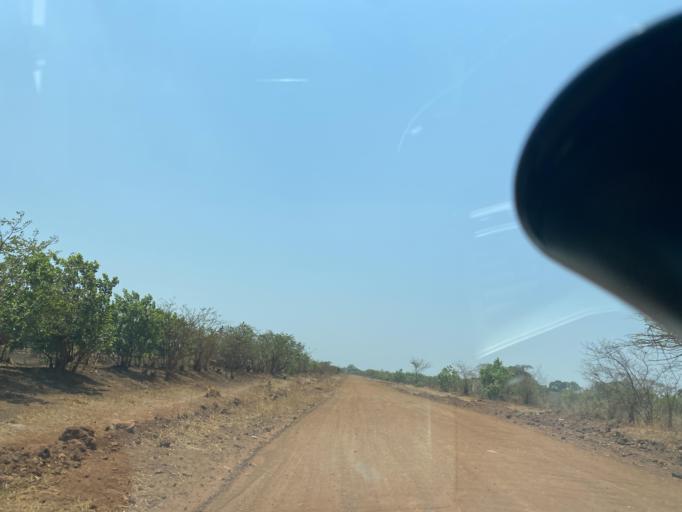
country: ZM
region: Lusaka
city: Lusaka
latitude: -15.4549
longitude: 27.9434
